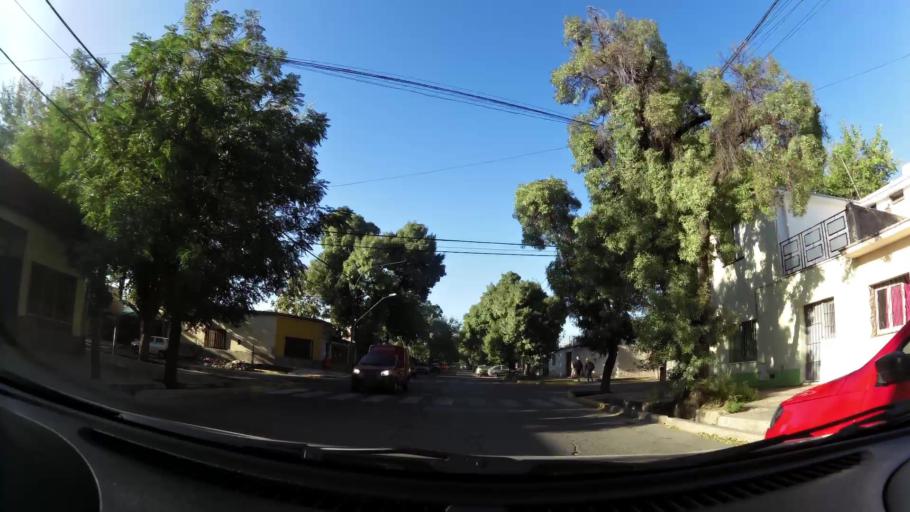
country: AR
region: Mendoza
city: Las Heras
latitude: -32.8700
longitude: -68.8231
